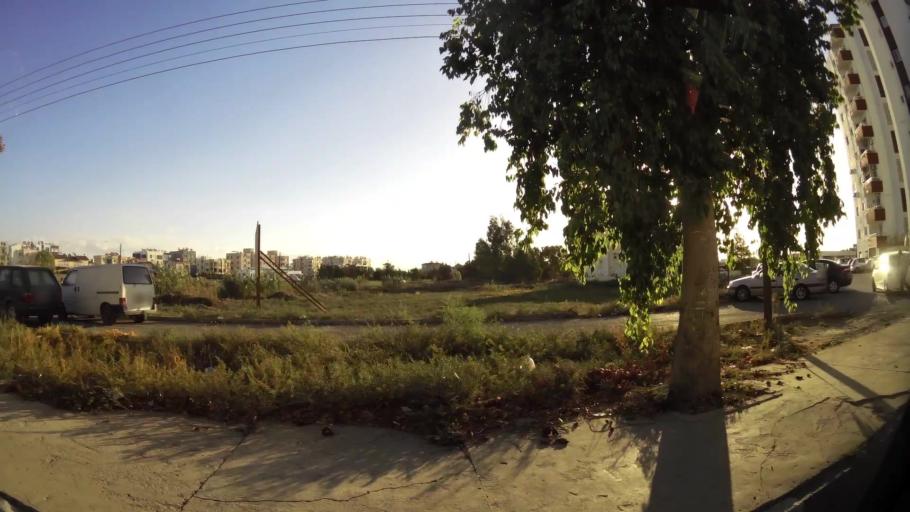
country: CY
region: Lefkosia
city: Nicosia
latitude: 35.2036
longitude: 33.3331
